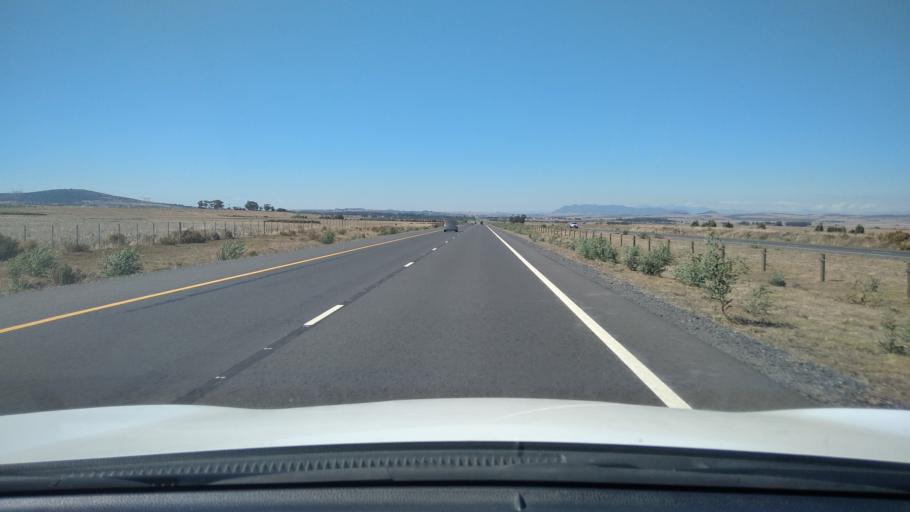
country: ZA
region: Western Cape
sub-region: City of Cape Town
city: Atlantis
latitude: -33.6502
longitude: 18.5679
